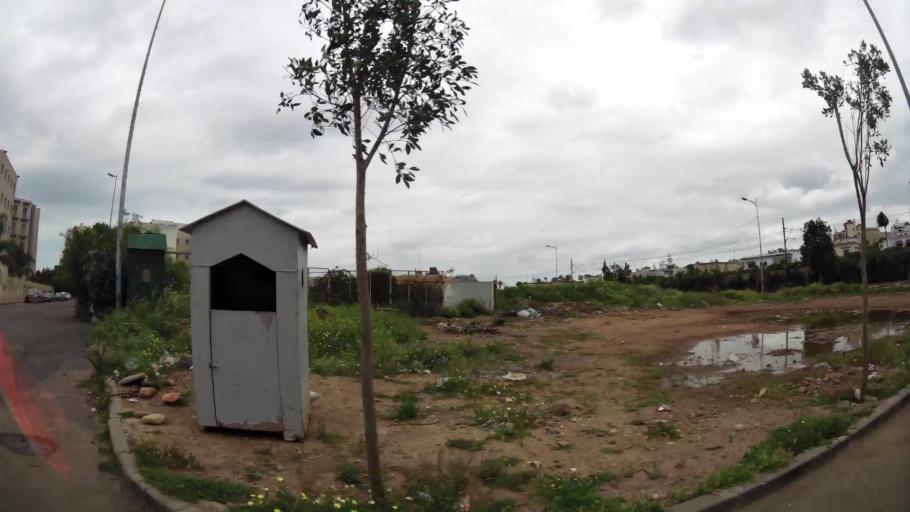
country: MA
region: Grand Casablanca
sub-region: Casablanca
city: Casablanca
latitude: 33.5494
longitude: -7.6359
